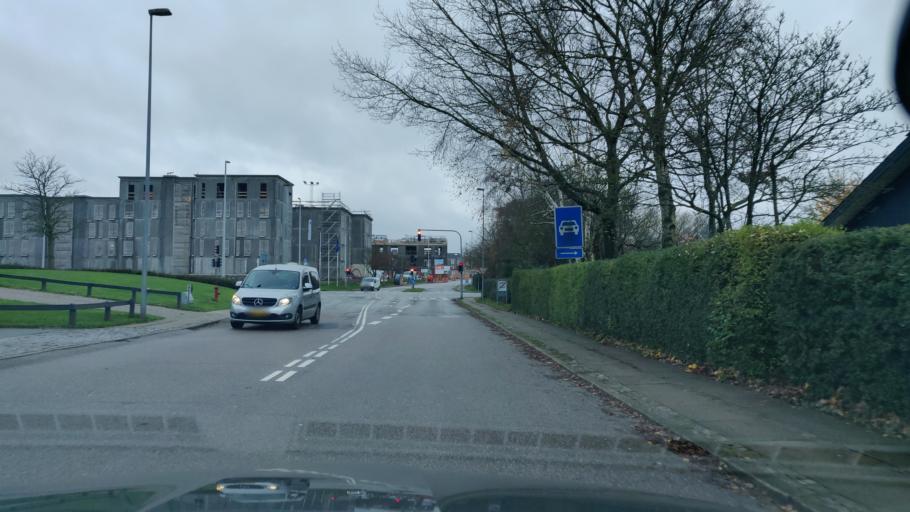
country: DK
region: North Denmark
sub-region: Alborg Kommune
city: Aalborg
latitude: 57.0160
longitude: 9.8889
